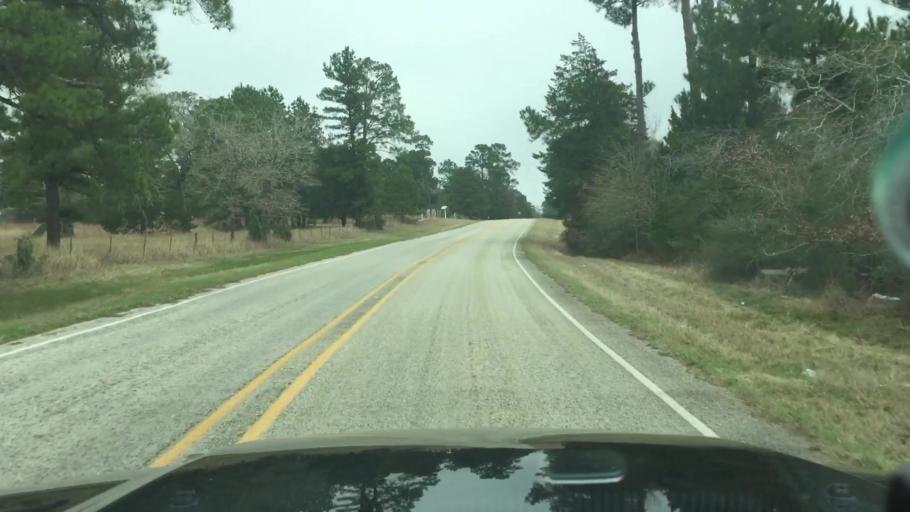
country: US
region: Texas
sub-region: Fayette County
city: La Grange
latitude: 30.0101
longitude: -96.9408
